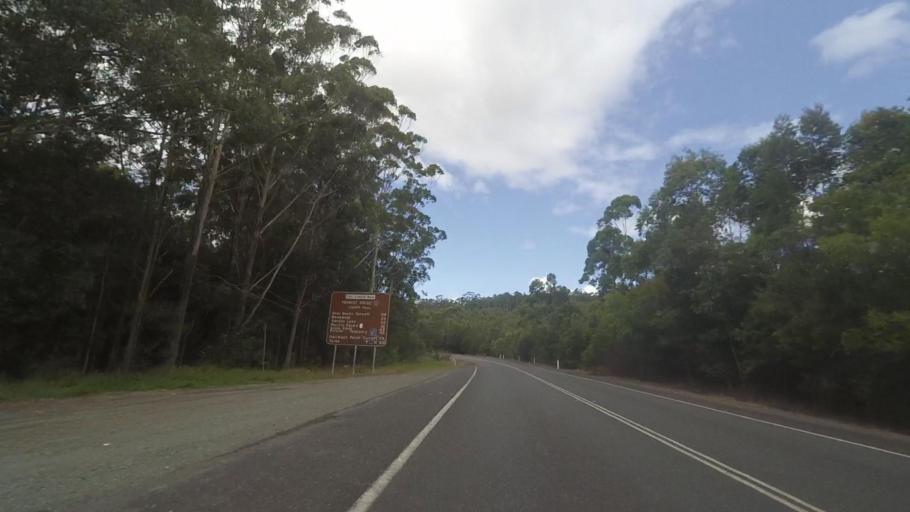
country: AU
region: New South Wales
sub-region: Great Lakes
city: Bulahdelah
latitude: -32.3881
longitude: 152.2393
